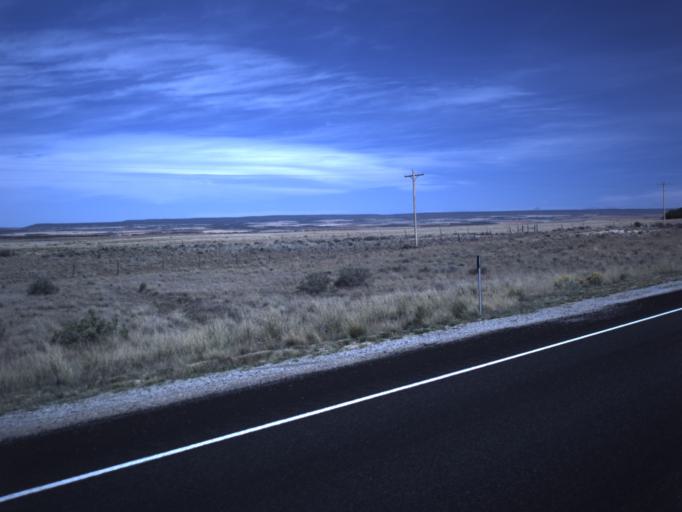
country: US
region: Colorado
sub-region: Dolores County
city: Dove Creek
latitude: 37.8335
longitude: -109.1012
